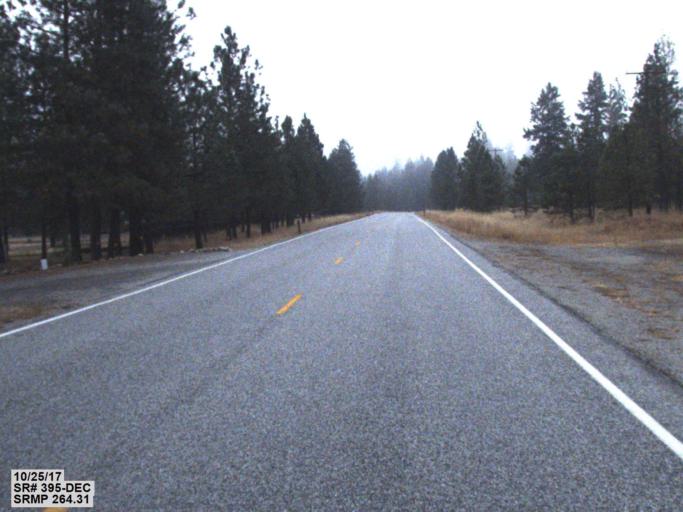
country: CA
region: British Columbia
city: Grand Forks
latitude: 48.9189
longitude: -118.2099
